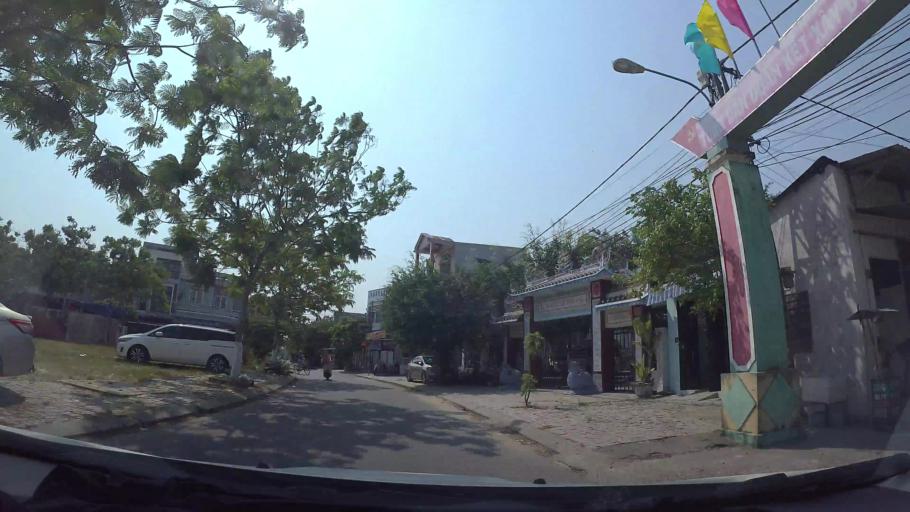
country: VN
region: Da Nang
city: Cam Le
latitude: 16.0109
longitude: 108.2031
